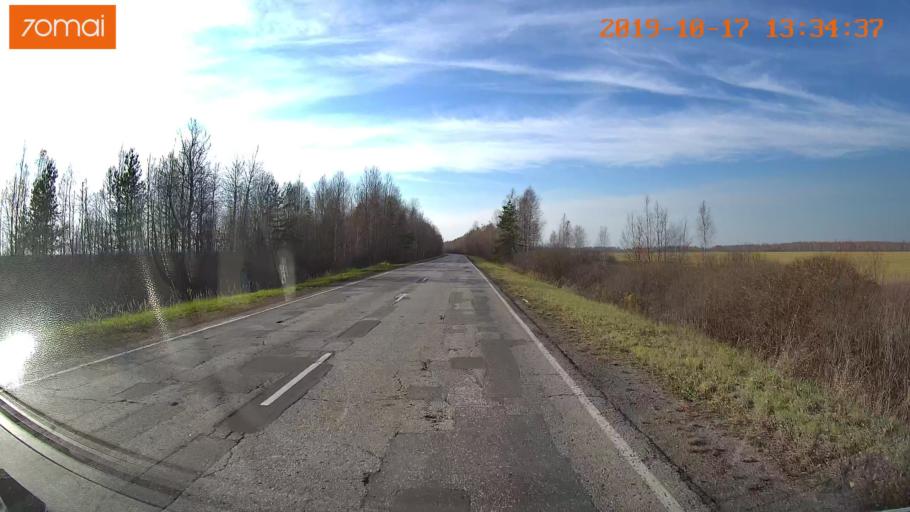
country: RU
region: Vladimir
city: Velikodvorskiy
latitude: 55.1441
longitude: 40.7111
